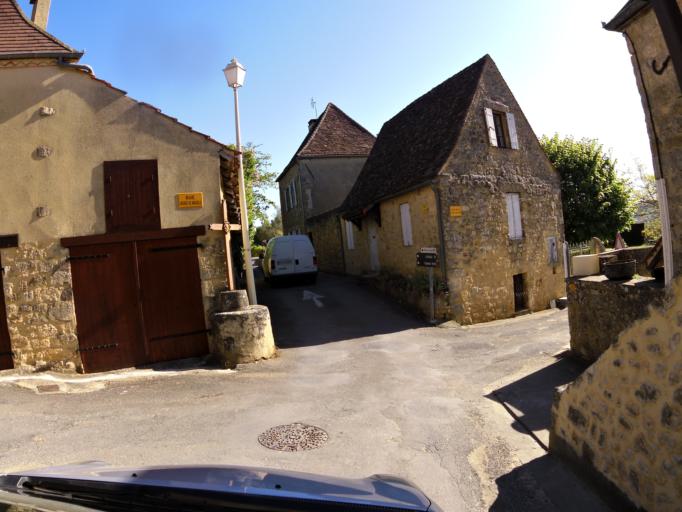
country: FR
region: Aquitaine
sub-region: Departement de la Dordogne
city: Domme
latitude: 44.8028
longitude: 1.2165
